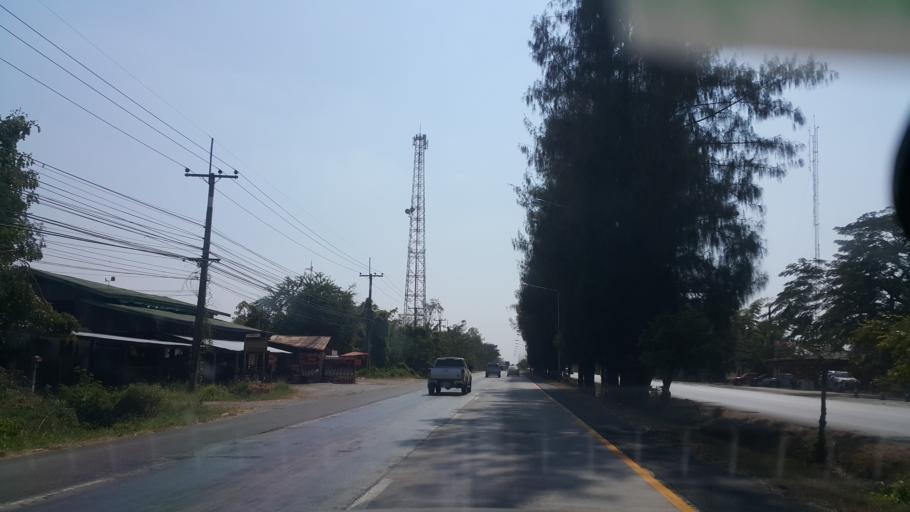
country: TH
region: Nakhon Ratchasima
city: Sida
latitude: 15.5386
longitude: 102.5460
